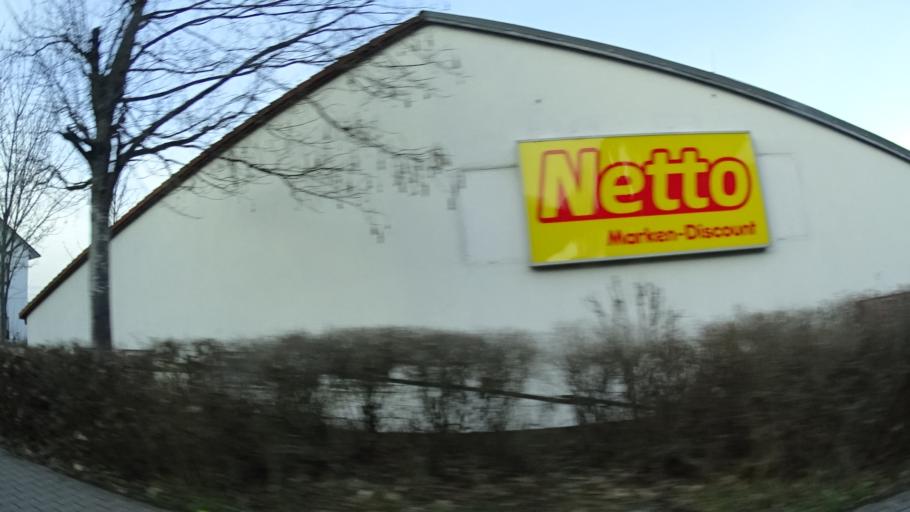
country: DE
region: Hesse
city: Reichelsheim
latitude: 49.7080
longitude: 8.8434
